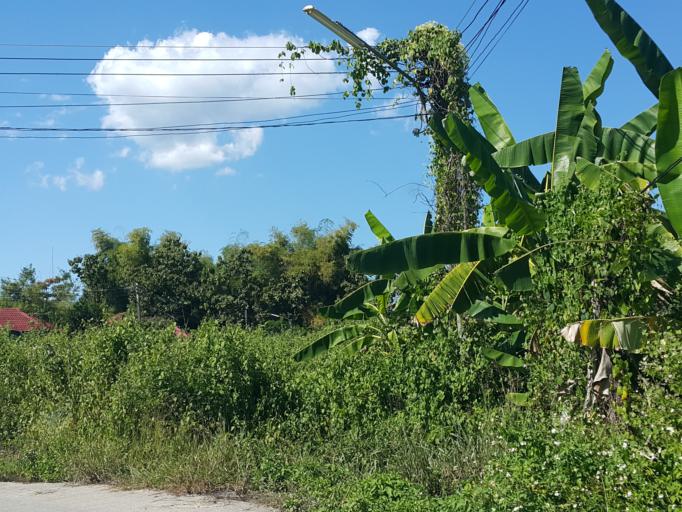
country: TH
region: Chiang Mai
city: San Sai
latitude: 18.8816
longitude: 99.1469
